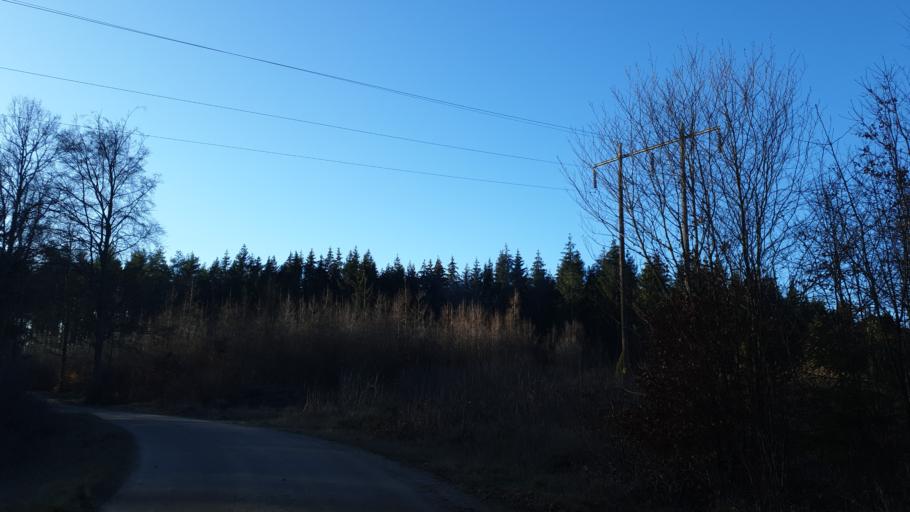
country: SE
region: Blekinge
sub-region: Karlskrona Kommun
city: Nattraby
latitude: 56.2597
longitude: 15.4123
